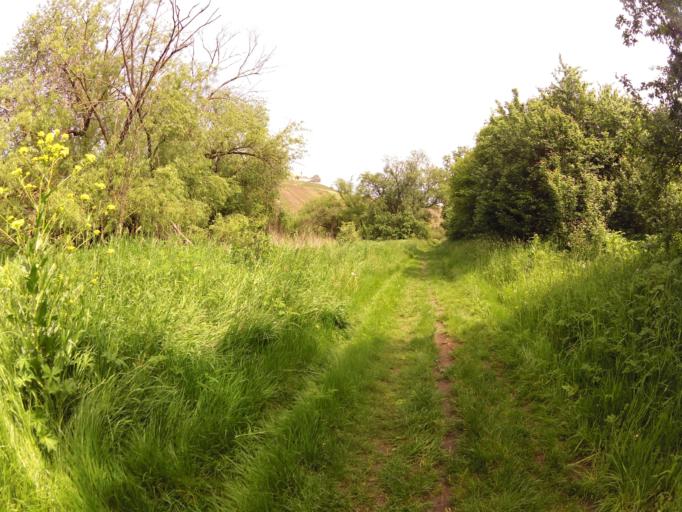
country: DE
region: Bavaria
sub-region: Regierungsbezirk Unterfranken
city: Nordheim
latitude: 49.8631
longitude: 10.1806
